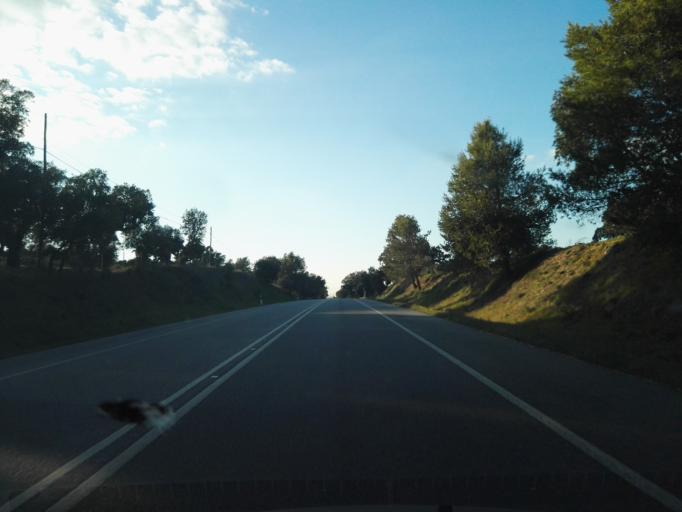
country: PT
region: Evora
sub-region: Montemor-O-Novo
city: Montemor-o-Novo
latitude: 38.6153
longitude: -8.0791
